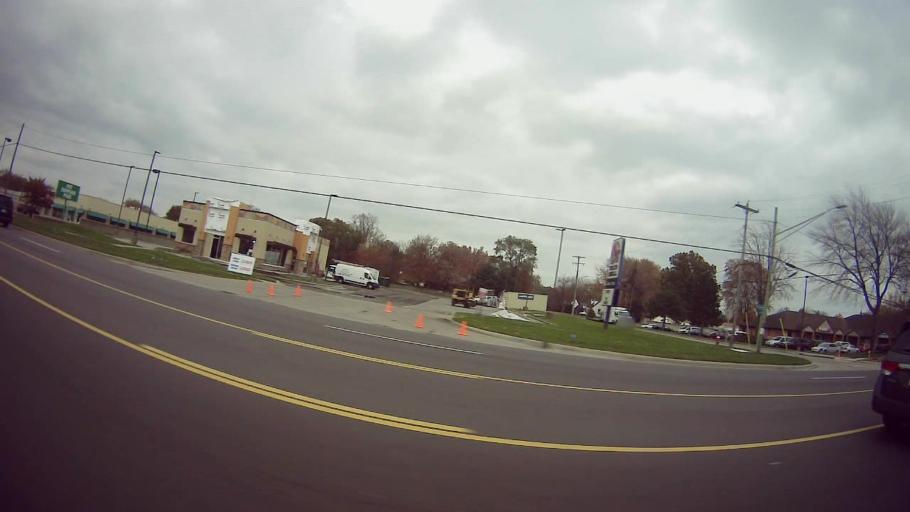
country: US
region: Michigan
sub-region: Macomb County
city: Center Line
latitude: 42.4858
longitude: -83.0064
